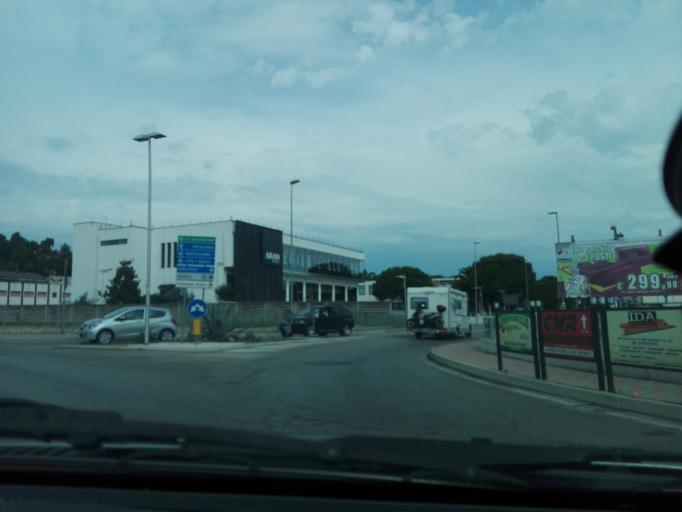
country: IT
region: Abruzzo
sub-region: Provincia di Pescara
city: San Martino Bassa
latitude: 42.5323
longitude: 14.1313
